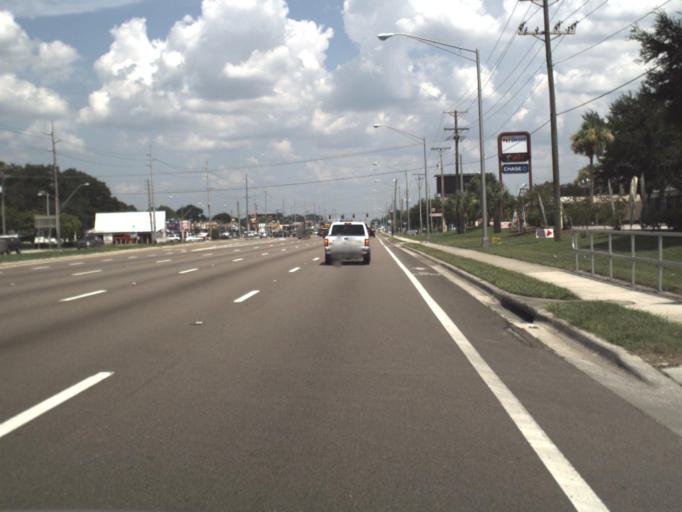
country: US
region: Florida
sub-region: Hillsborough County
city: Brandon
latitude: 27.9376
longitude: -82.3011
